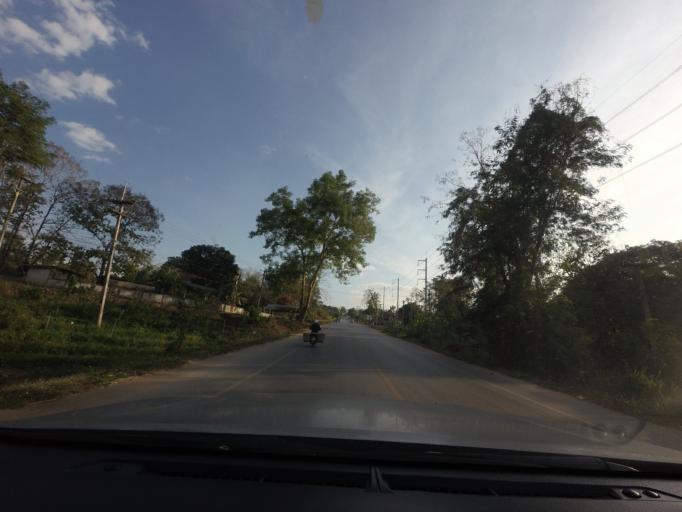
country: TH
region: Mae Hong Son
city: Mae Hi
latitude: 19.3438
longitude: 98.4329
